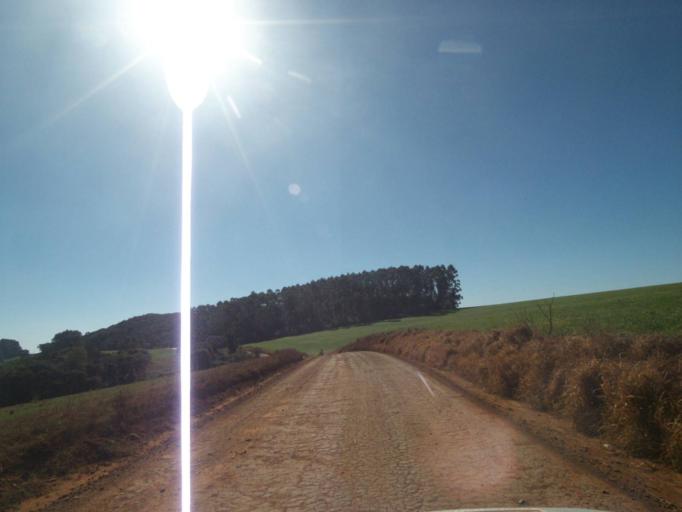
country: BR
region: Parana
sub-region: Tibagi
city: Tibagi
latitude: -24.5987
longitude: -50.6023
